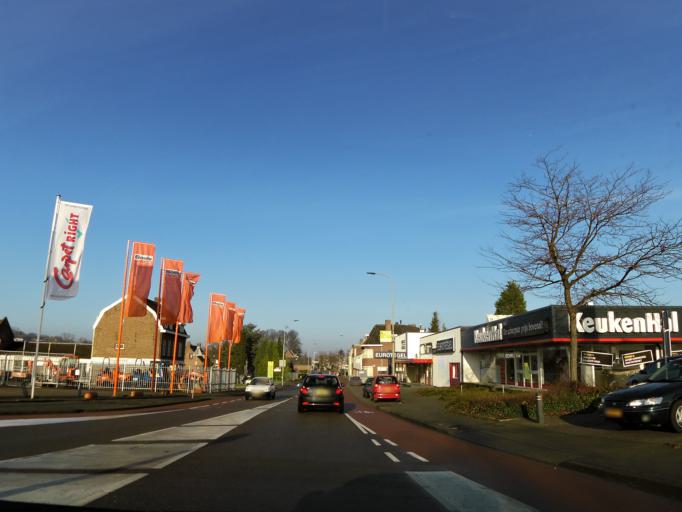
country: NL
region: Limburg
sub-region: Gemeente Heerlen
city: Heerlen
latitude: 50.8644
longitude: 6.0035
